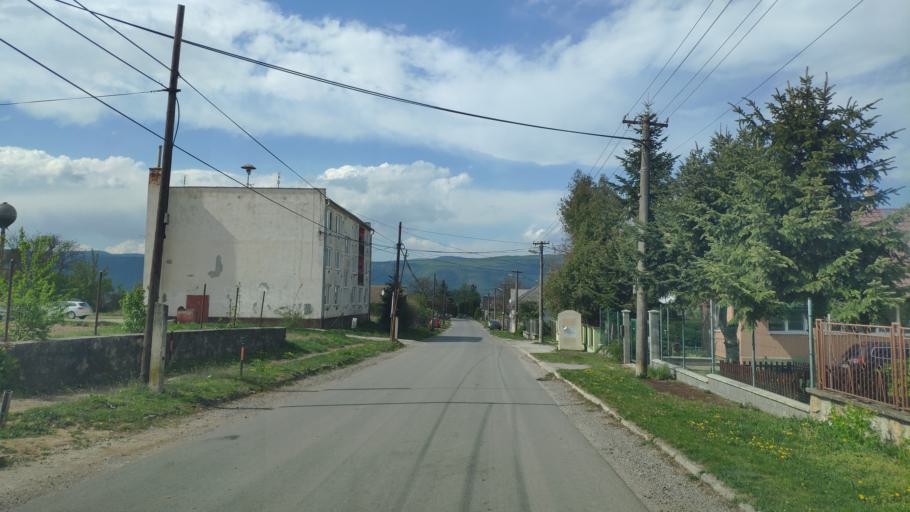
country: SK
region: Kosicky
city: Moldava nad Bodvou
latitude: 48.5821
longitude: 20.9227
